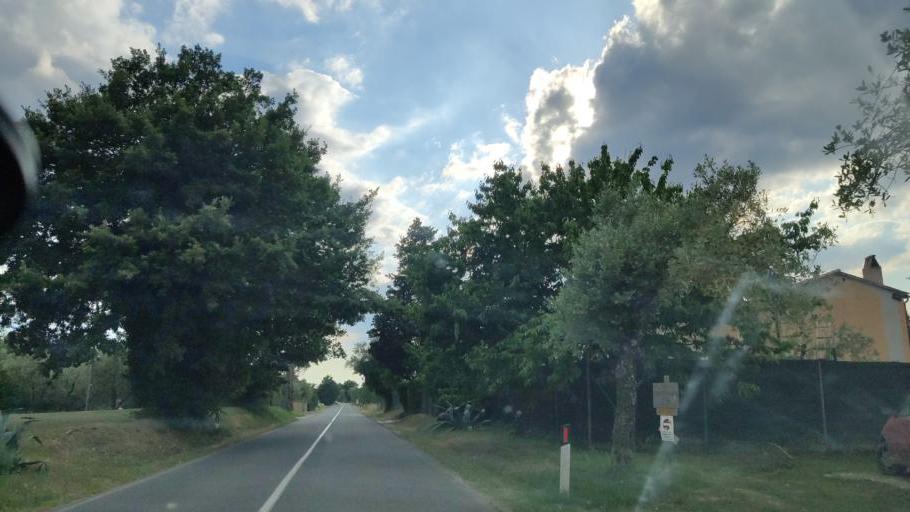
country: IT
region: Umbria
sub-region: Provincia di Terni
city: Giove
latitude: 42.5132
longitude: 12.3497
